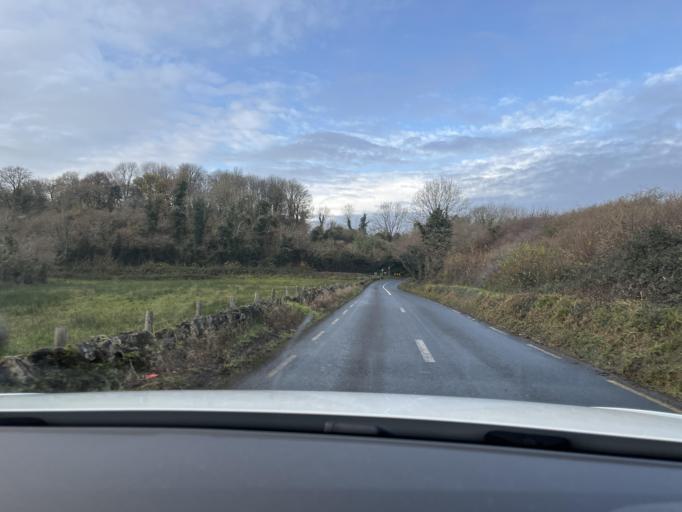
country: IE
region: Connaught
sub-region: Sligo
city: Sligo
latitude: 54.2654
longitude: -8.3648
